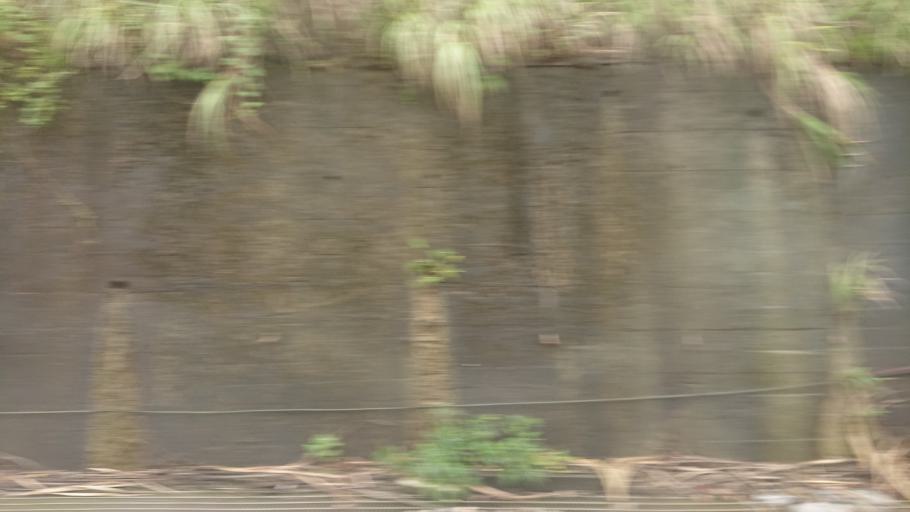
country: TW
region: Taiwan
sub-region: Keelung
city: Keelung
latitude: 25.0996
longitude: 121.7230
